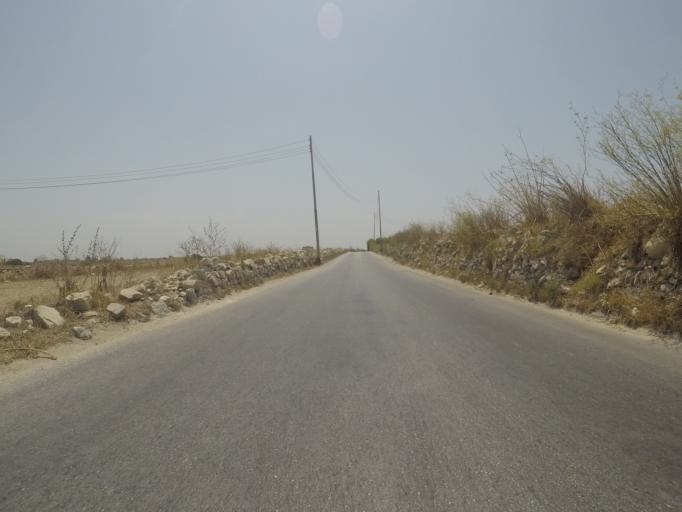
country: MT
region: L-Imdina
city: Imdina
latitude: 35.8772
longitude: 14.4126
